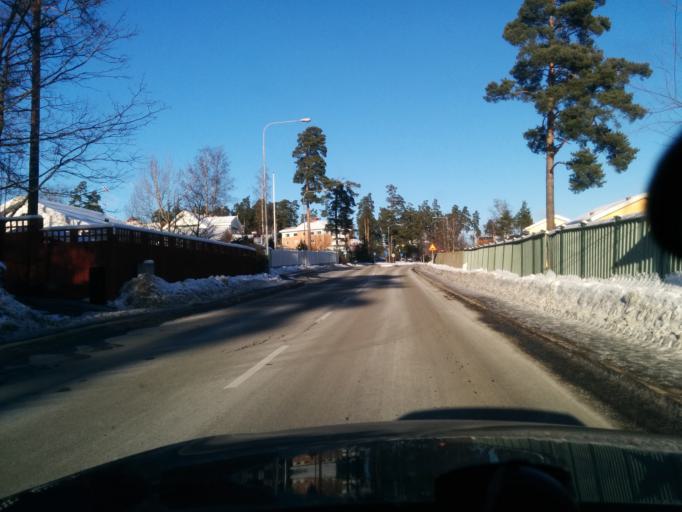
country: SE
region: Stockholm
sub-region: Taby Kommun
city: Taby
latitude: 59.4645
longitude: 18.0880
